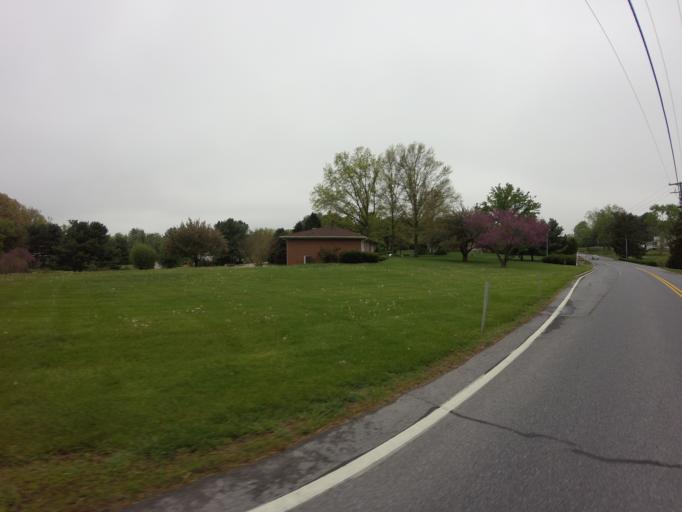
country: US
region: Maryland
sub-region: Baltimore County
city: Hunt Valley
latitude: 39.5901
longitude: -76.6948
